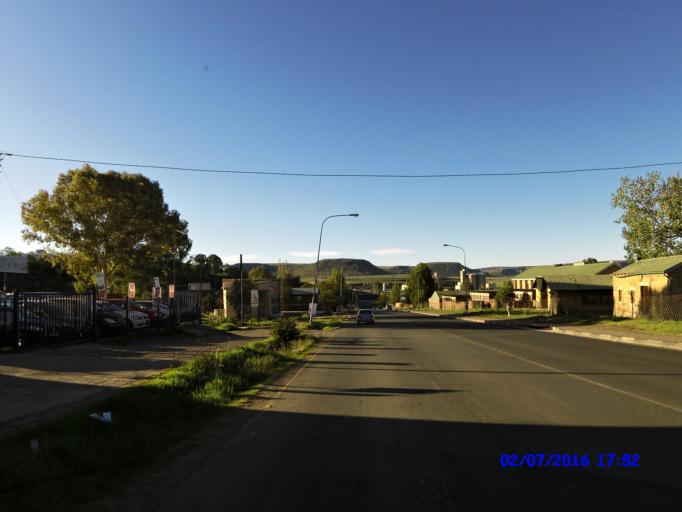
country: LS
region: Maseru
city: Maseru
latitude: -29.3059
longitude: 27.4841
